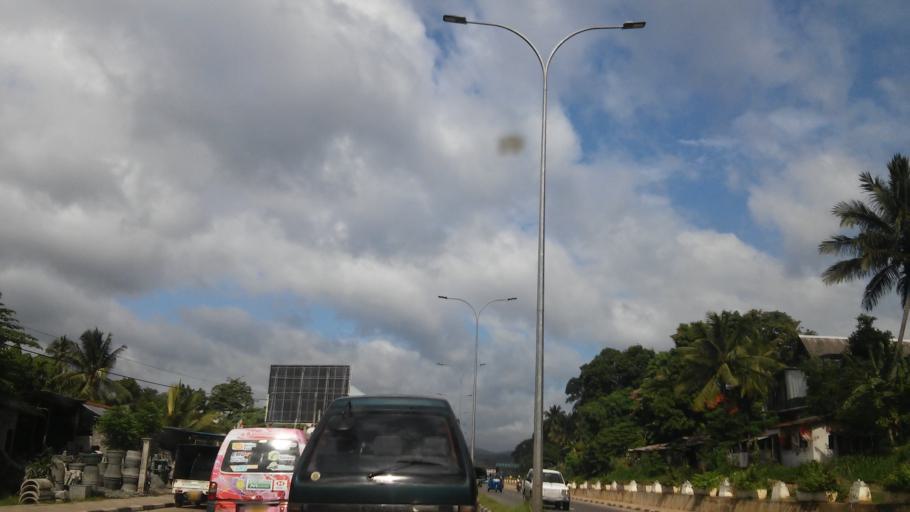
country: LK
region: Central
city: Kandy
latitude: 7.2754
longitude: 80.6145
